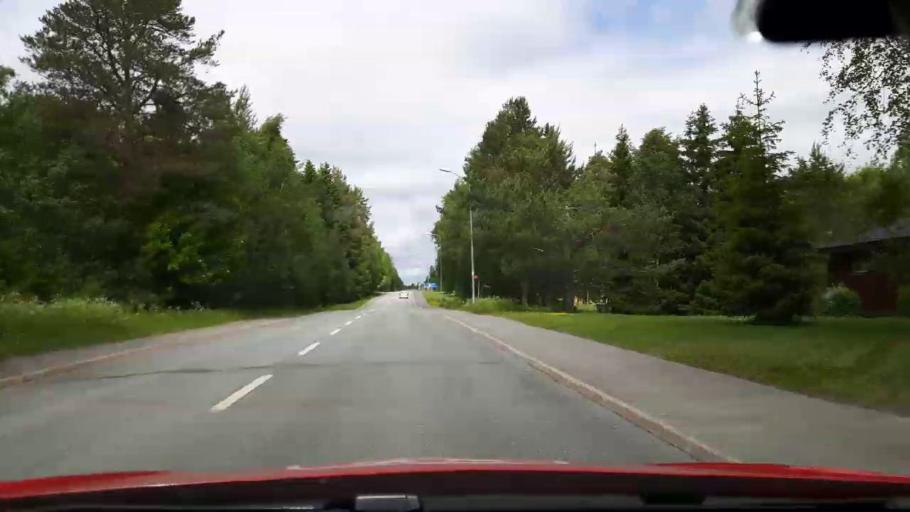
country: SE
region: Jaemtland
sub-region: Krokoms Kommun
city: Krokom
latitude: 63.3318
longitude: 14.4462
